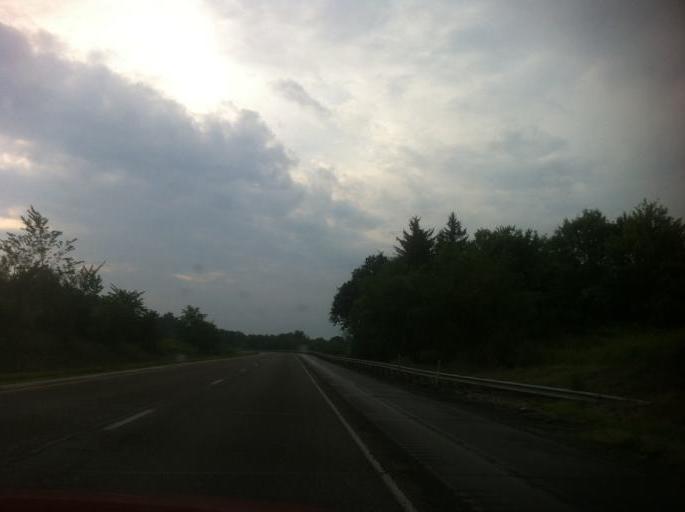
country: US
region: Pennsylvania
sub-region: Clarion County
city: Knox
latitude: 41.1949
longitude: -79.6186
